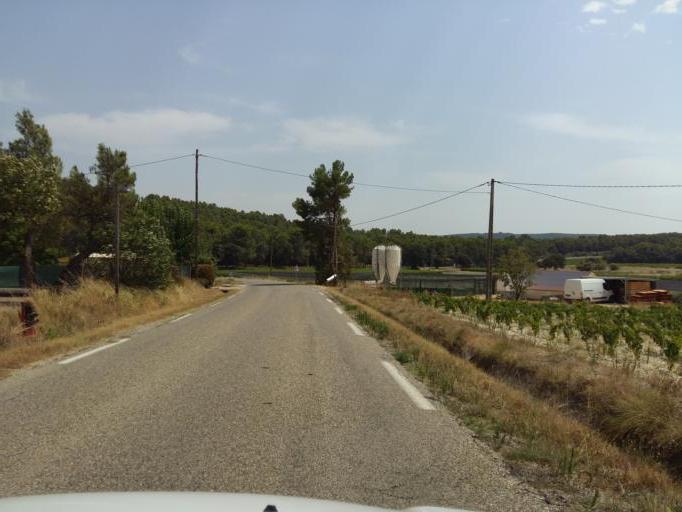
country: FR
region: Rhone-Alpes
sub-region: Departement de la Drome
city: Rochegude
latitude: 44.2514
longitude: 4.7958
